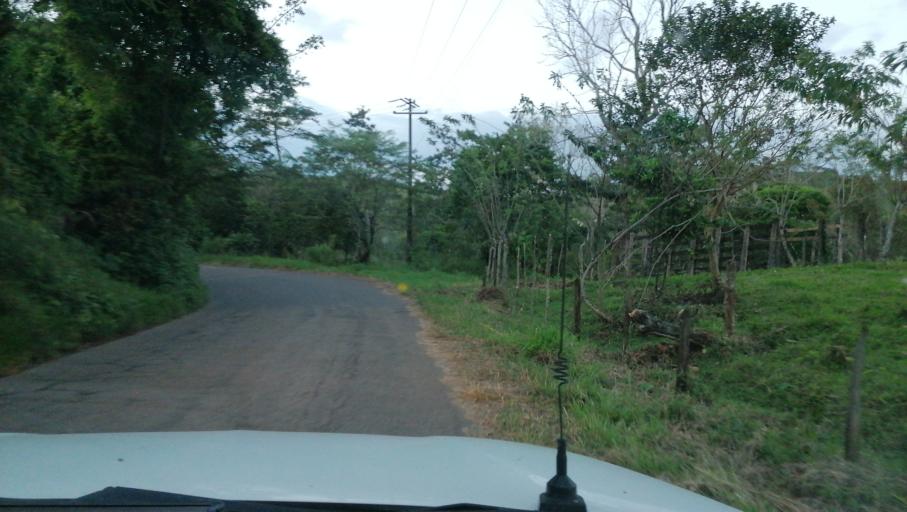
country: MX
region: Chiapas
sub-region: Ostuacan
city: Nuevo Juan del Grijalva
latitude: 17.4424
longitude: -93.3521
